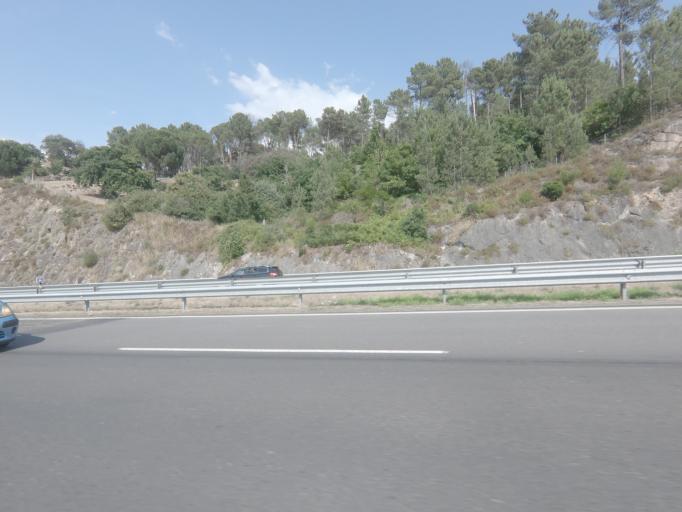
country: ES
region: Galicia
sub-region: Provincia de Ourense
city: Ourense
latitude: 42.2956
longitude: -7.8776
